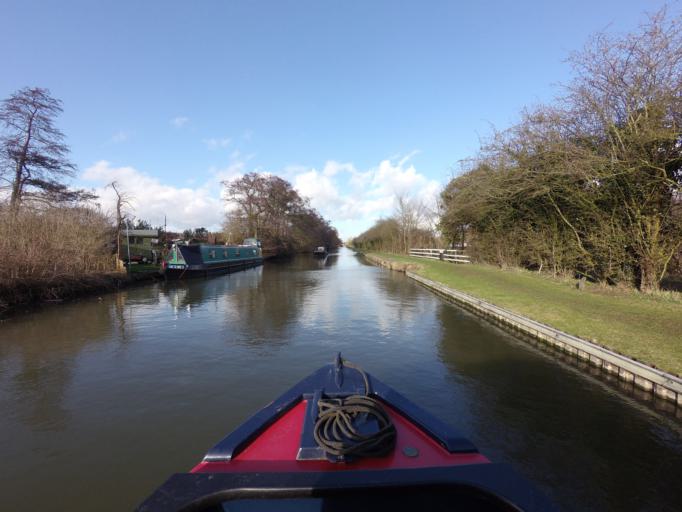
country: GB
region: England
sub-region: Northamptonshire
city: Long Buckby
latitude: 52.2690
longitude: -1.0938
